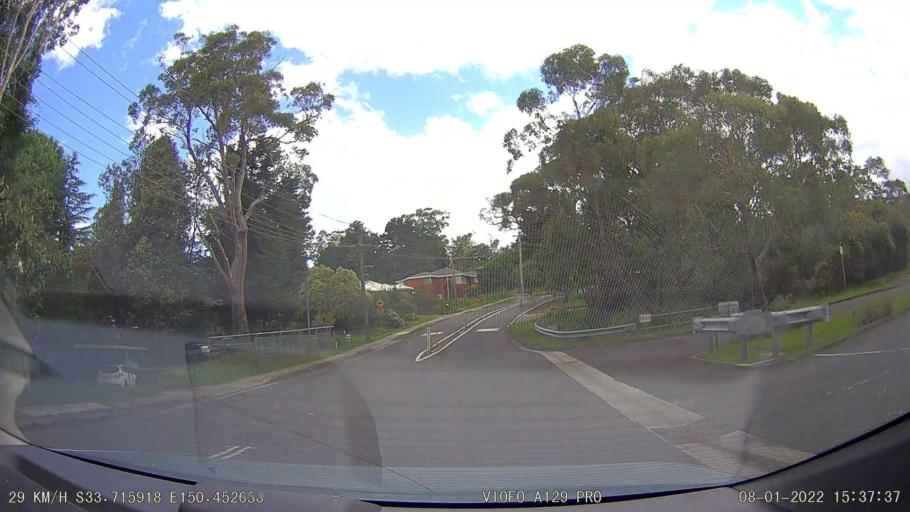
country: AU
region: New South Wales
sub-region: Blue Mountains Municipality
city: Hazelbrook
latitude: -33.7158
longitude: 150.4526
